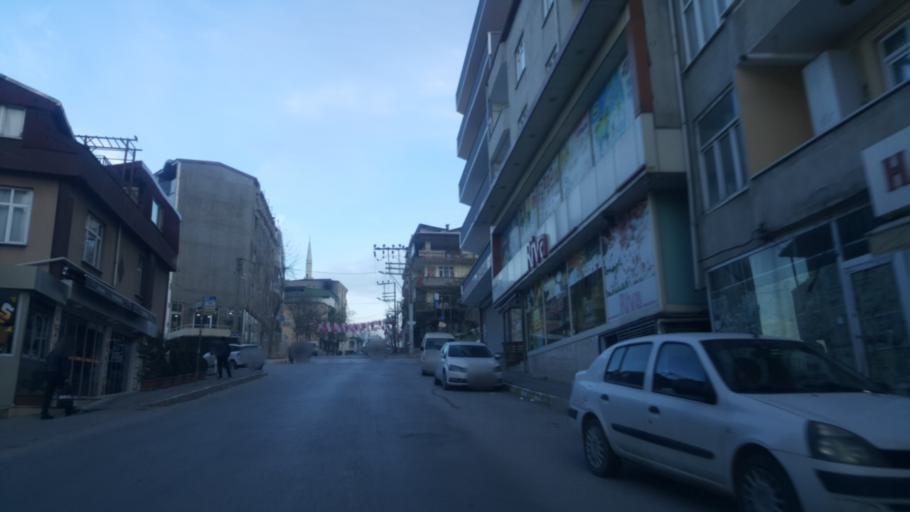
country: TR
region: Kocaeli
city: Tavsancil
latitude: 40.7863
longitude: 29.5405
